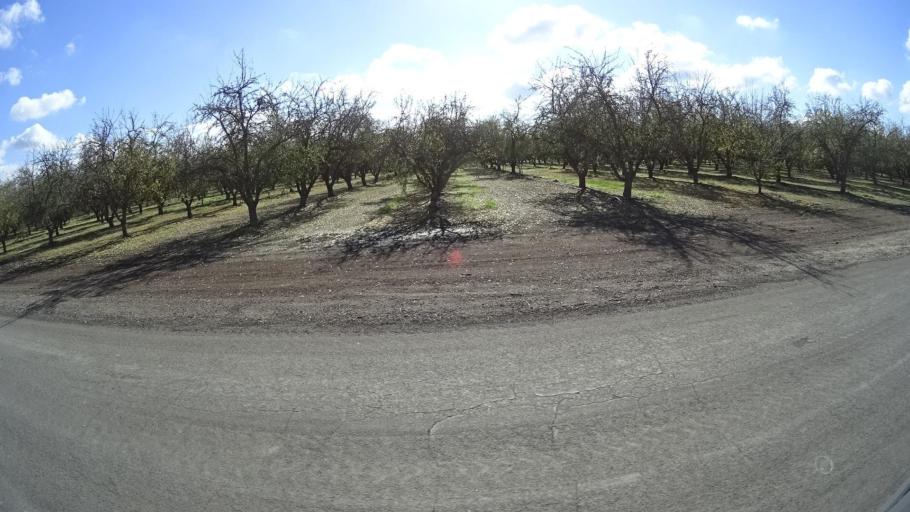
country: US
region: California
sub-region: Kern County
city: Delano
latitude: 35.7322
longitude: -119.3240
